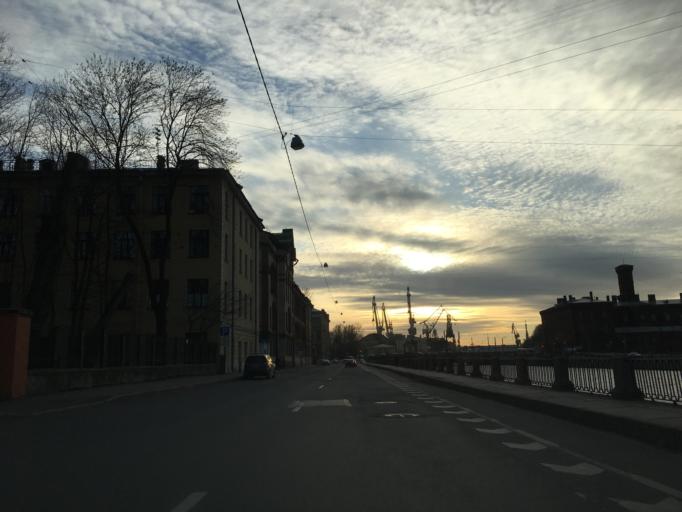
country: RU
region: St.-Petersburg
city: Admiralteisky
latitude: 59.9159
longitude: 30.2847
